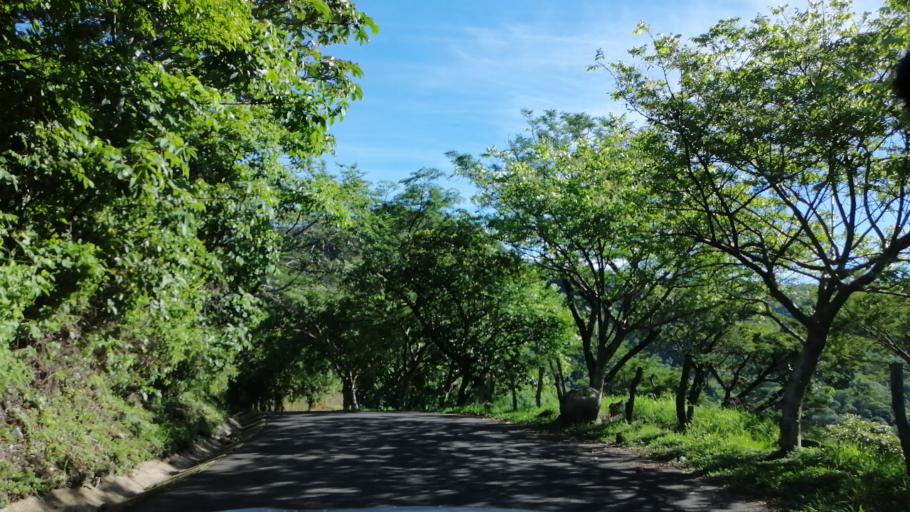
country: SV
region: Morazan
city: Corinto
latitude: 13.7905
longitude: -88.0124
